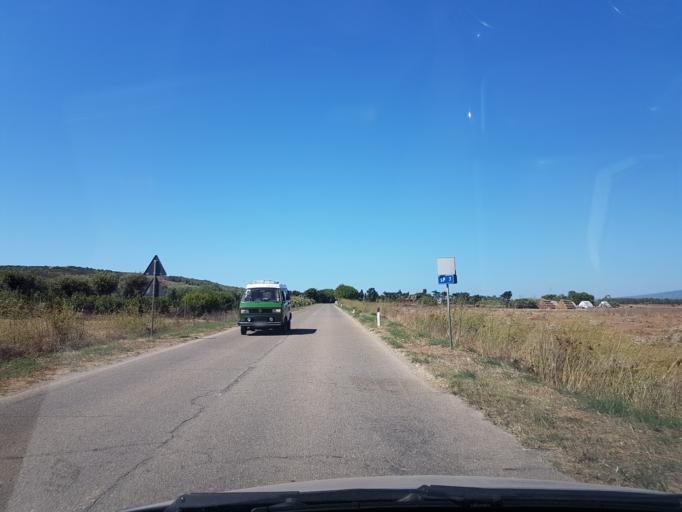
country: IT
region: Sardinia
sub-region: Provincia di Oristano
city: Cabras
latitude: 39.9405
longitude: 8.4579
